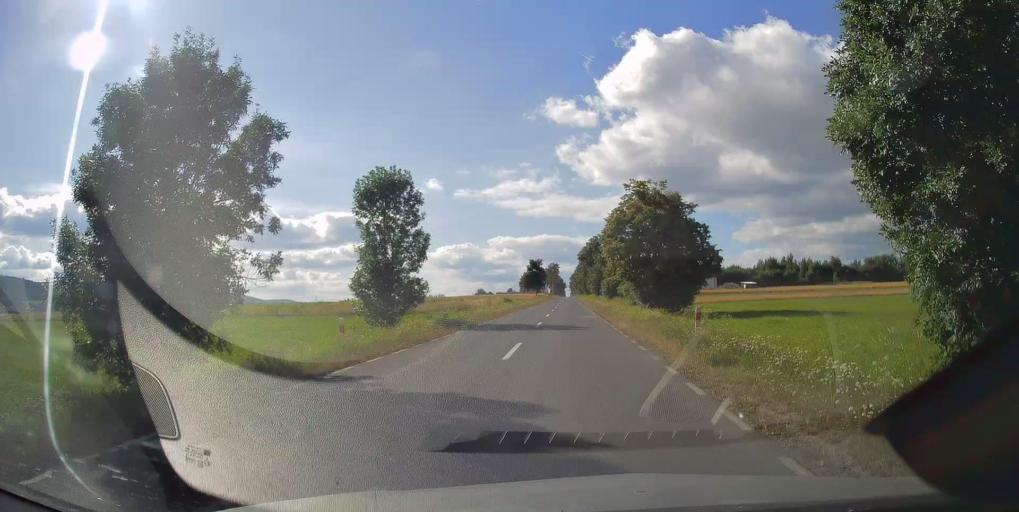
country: PL
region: Swietokrzyskie
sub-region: Powiat kielecki
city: Bodzentyn
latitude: 50.9545
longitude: 20.9185
